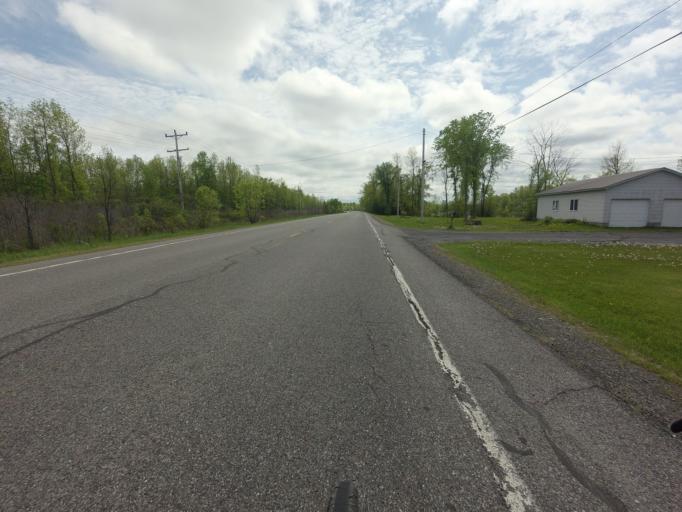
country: CA
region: Ontario
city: Cornwall
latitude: 44.9658
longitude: -74.6652
